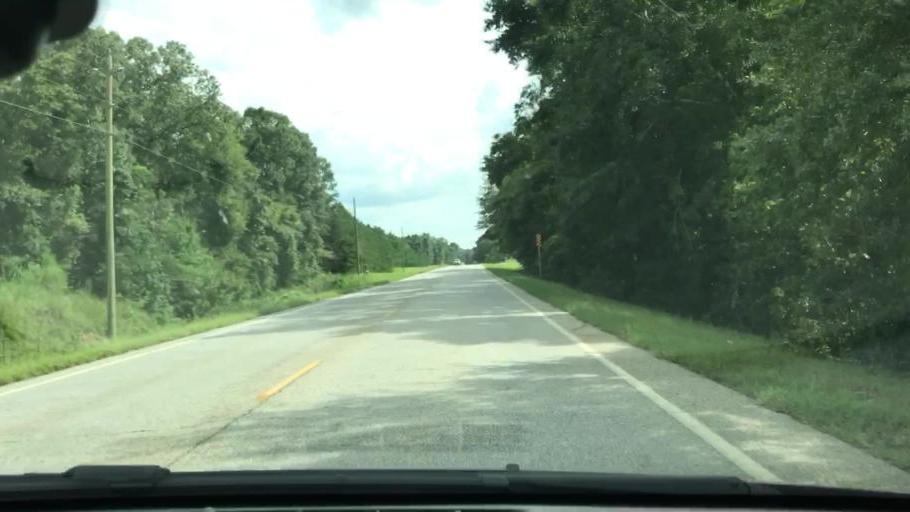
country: US
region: Georgia
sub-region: Clay County
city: Fort Gaines
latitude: 31.7096
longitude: -85.0415
